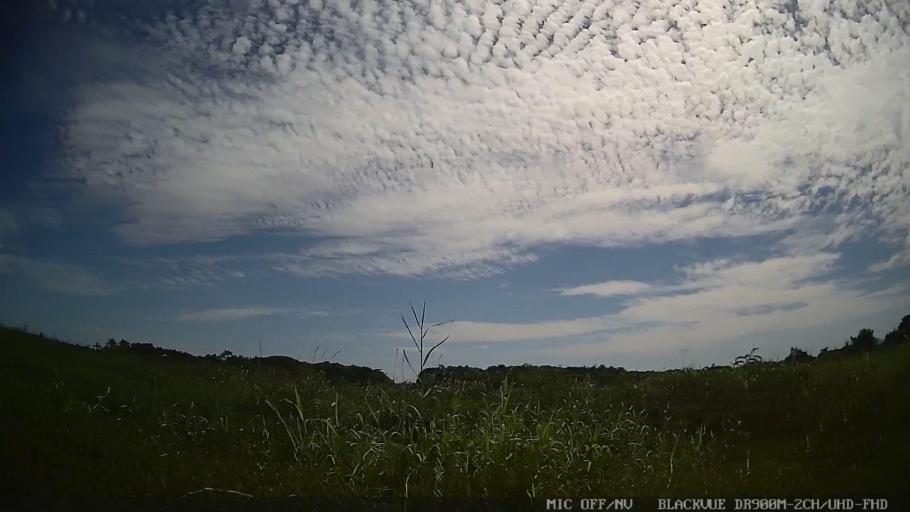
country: BR
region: Sao Paulo
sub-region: Iguape
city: Iguape
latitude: -24.7928
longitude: -47.6217
